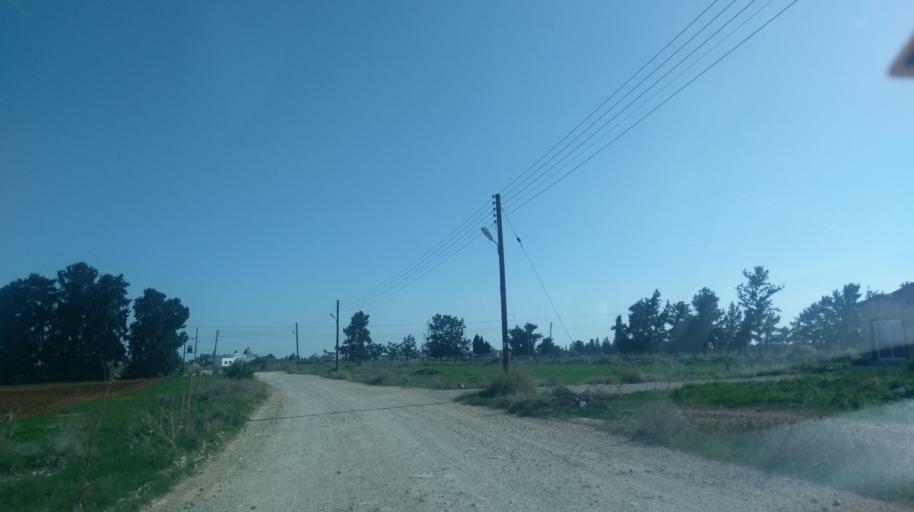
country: CY
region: Ammochostos
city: Trikomo
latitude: 35.2403
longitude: 33.8504
